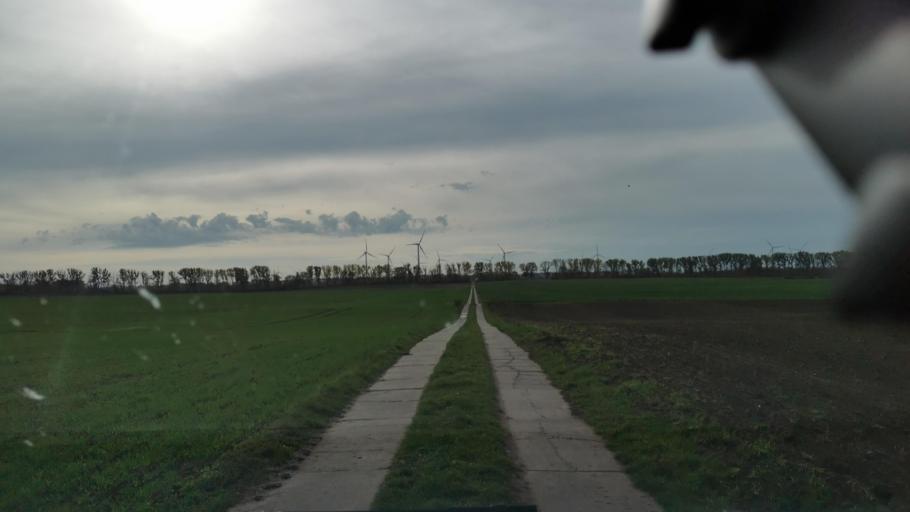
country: DE
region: Brandenburg
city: Eberswalde
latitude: 52.7801
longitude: 13.8559
